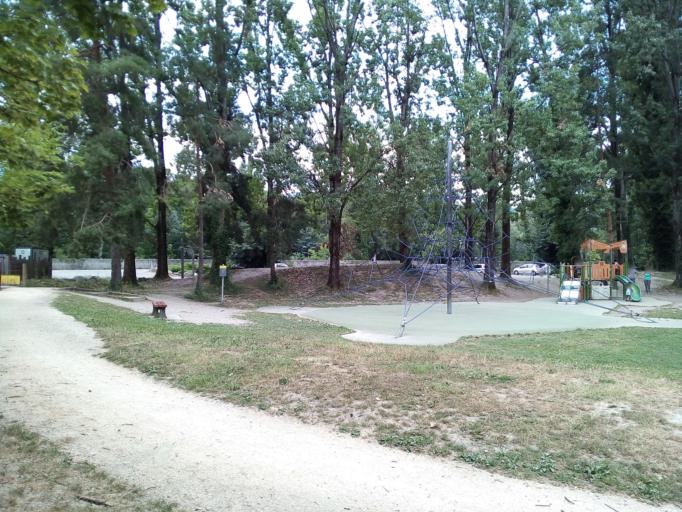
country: FR
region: Rhone-Alpes
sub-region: Departement de l'Isere
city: Corenc
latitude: 45.2007
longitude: 5.7702
